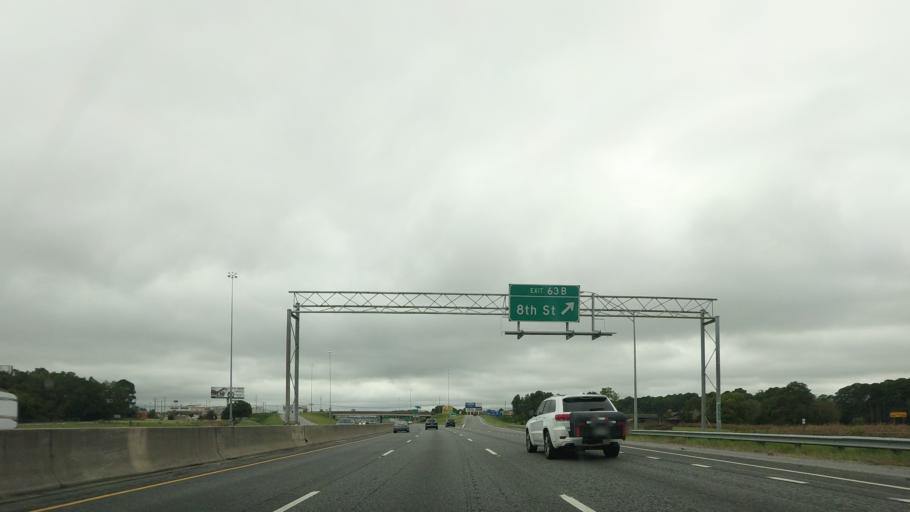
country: US
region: Georgia
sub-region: Tift County
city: Tifton
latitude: 31.4665
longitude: -83.5295
